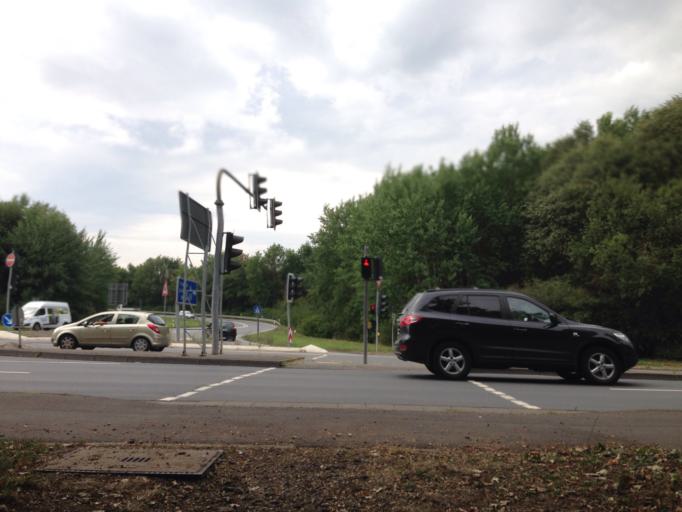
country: DE
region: Hesse
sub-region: Regierungsbezirk Giessen
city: Giessen
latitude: 50.5683
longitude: 8.7000
